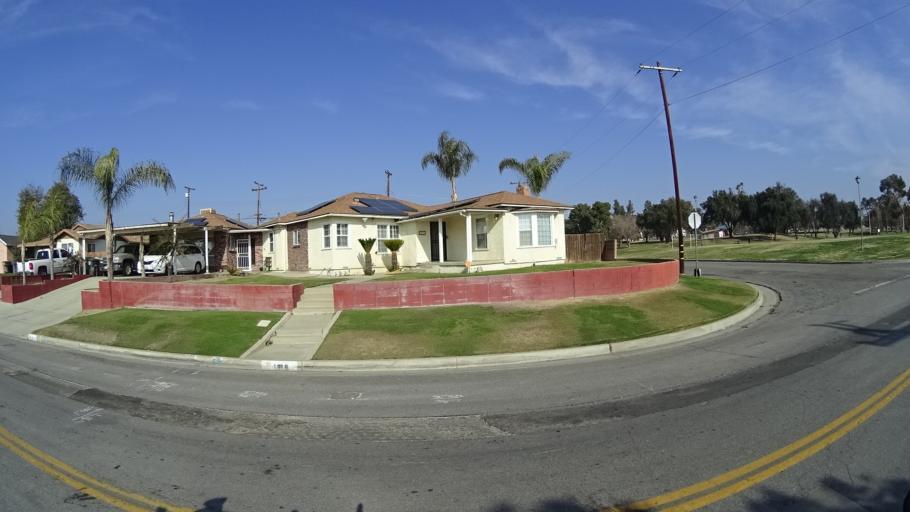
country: US
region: California
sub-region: Kern County
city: Bakersfield
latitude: 35.3865
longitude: -118.9705
